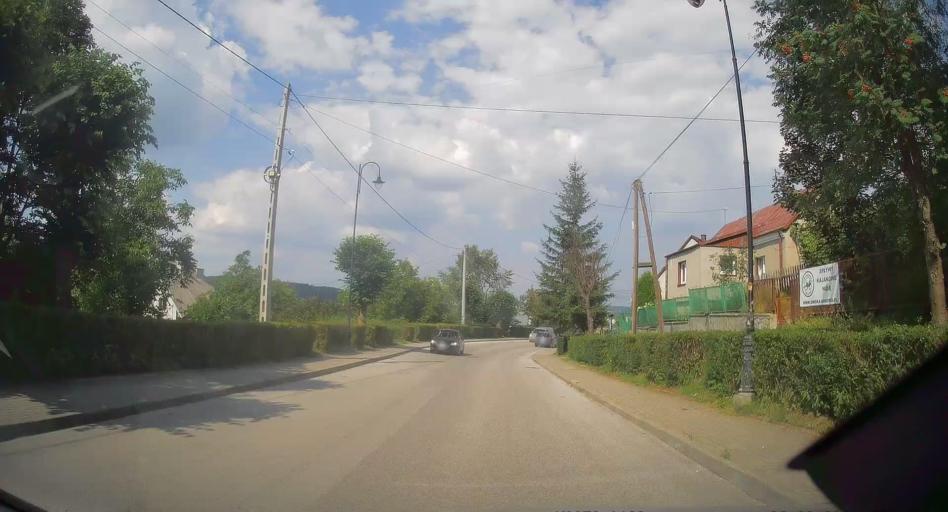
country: PL
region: Swietokrzyskie
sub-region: Powiat kielecki
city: Checiny
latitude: 50.7996
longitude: 20.4578
